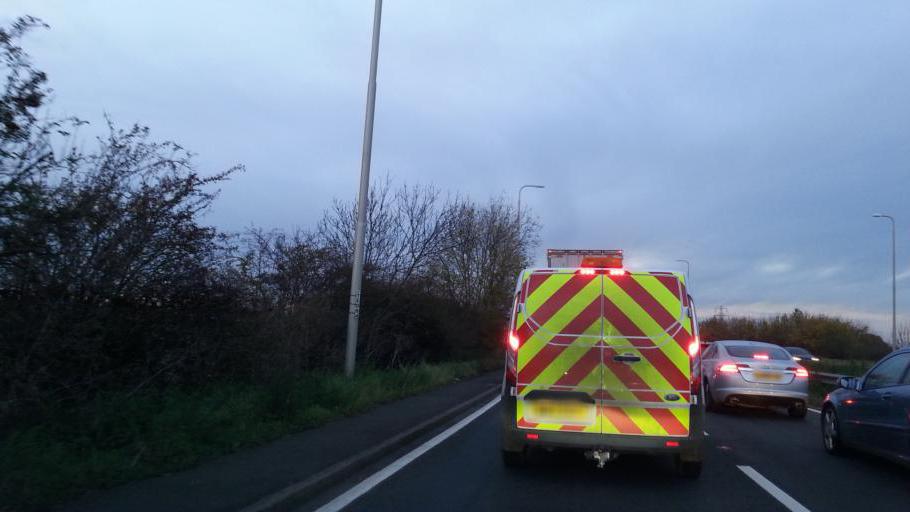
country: GB
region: England
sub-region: Central Bedfordshire
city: Tempsford
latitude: 52.1749
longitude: -0.2998
